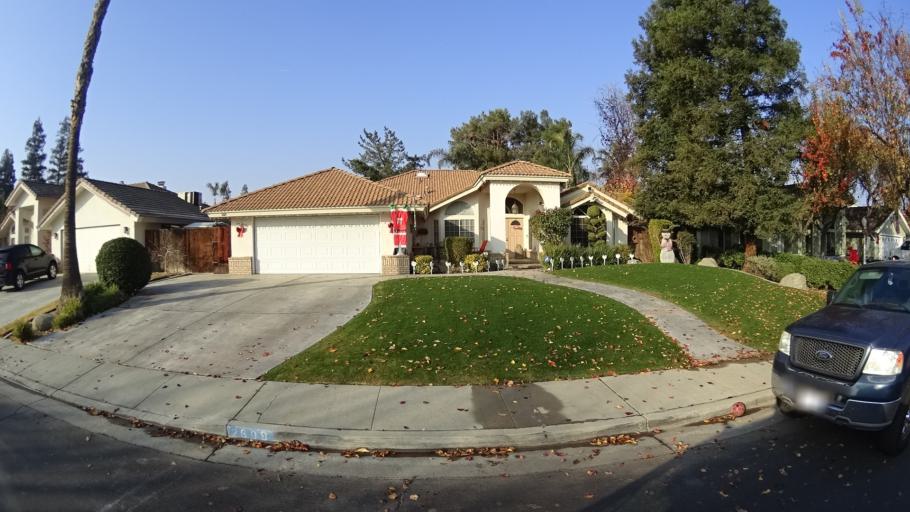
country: US
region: California
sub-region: Kern County
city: Greenacres
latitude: 35.3298
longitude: -119.1011
